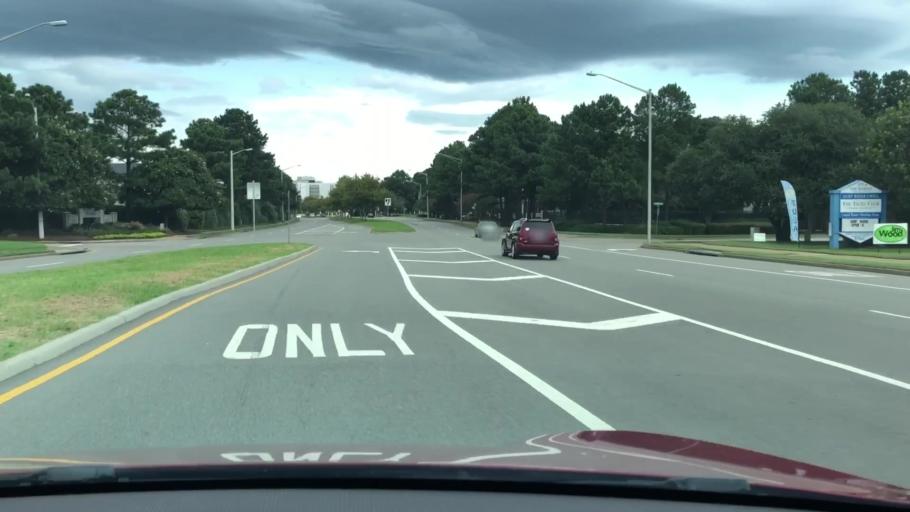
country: US
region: Virginia
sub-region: City of Virginia Beach
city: Virginia Beach
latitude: 36.9074
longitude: -76.0674
